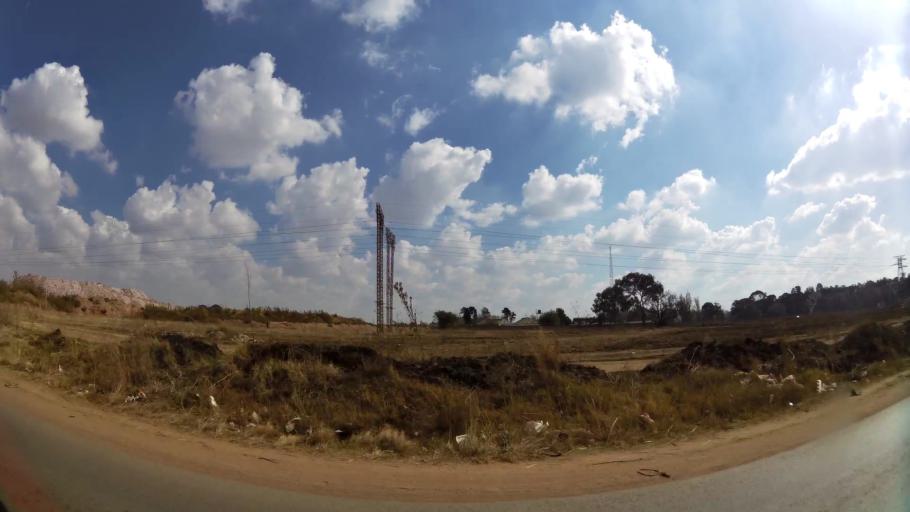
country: ZA
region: Gauteng
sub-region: City of Johannesburg Metropolitan Municipality
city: Roodepoort
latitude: -26.1845
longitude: 27.8689
